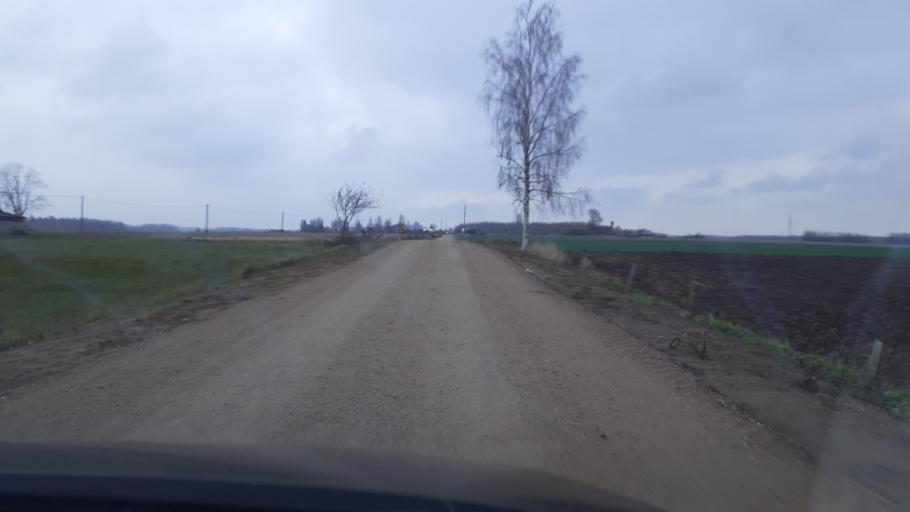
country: LV
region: Talsu Rajons
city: Sabile
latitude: 56.9358
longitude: 22.4180
